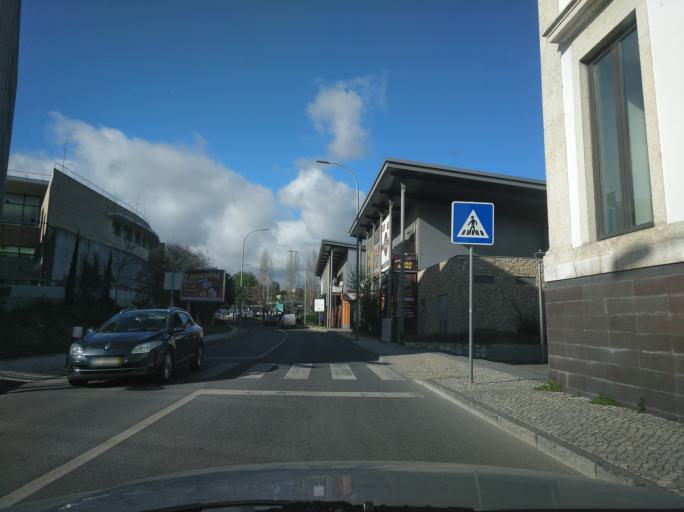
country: PT
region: Lisbon
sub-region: Loures
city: Loures
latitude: 38.8250
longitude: -9.1619
